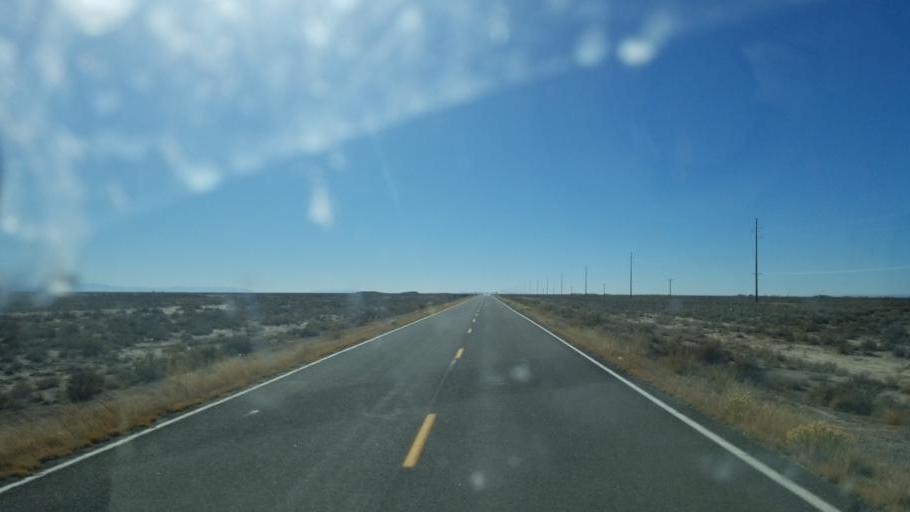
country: US
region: Colorado
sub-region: Saguache County
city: Center
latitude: 37.8875
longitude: -105.8961
